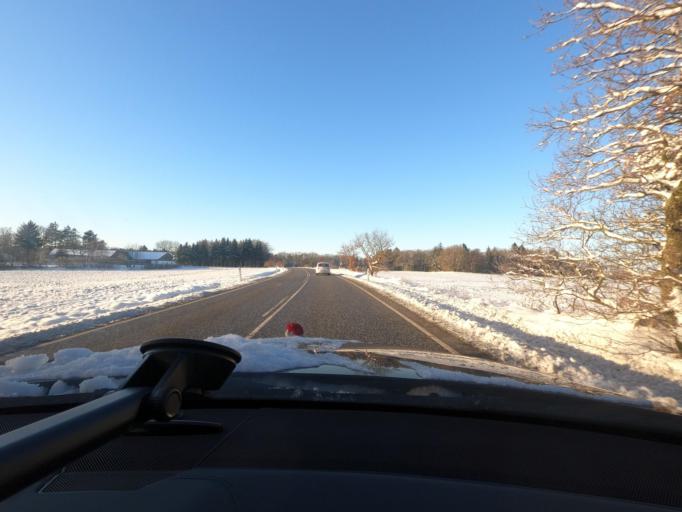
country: DK
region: South Denmark
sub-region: Tonder Kommune
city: Logumkloster
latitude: 55.1800
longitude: 8.9236
